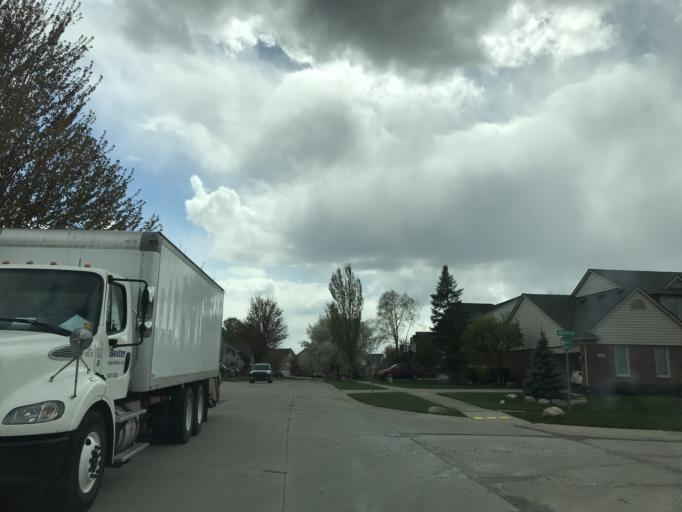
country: US
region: Michigan
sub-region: Wayne County
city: Plymouth
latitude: 42.3716
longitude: -83.5405
